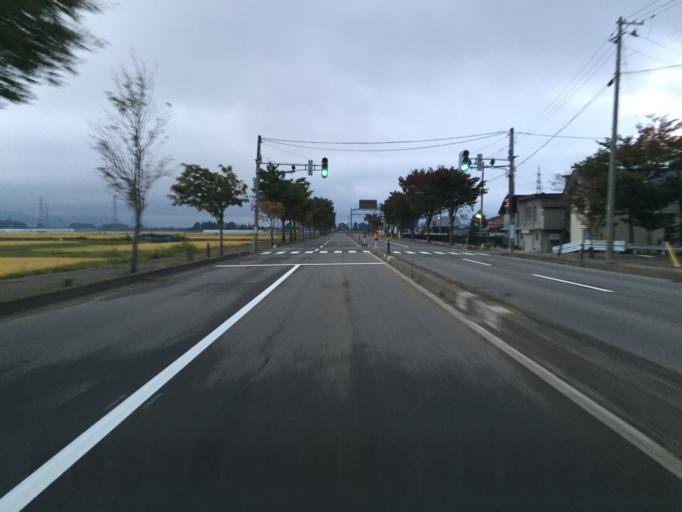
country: JP
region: Fukushima
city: Inawashiro
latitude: 37.5535
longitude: 140.1132
